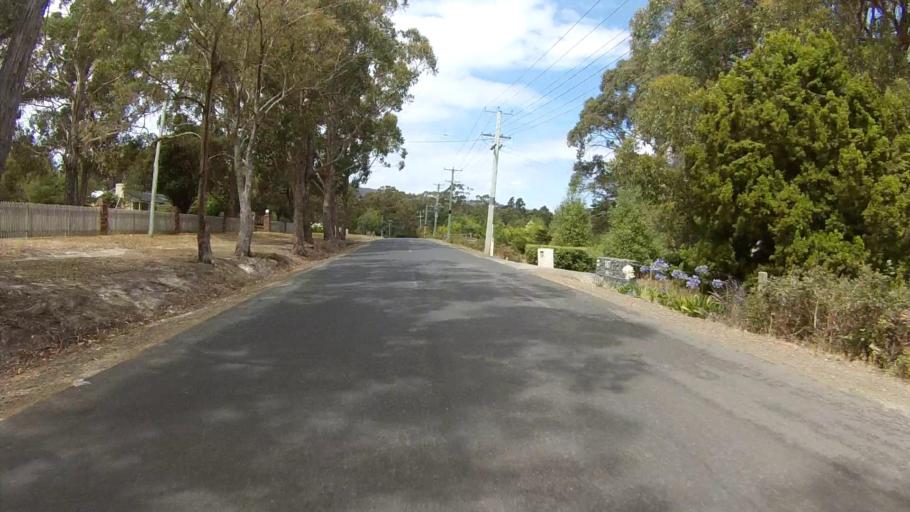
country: AU
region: Tasmania
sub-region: Kingborough
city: Blackmans Bay
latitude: -43.0128
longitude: 147.2887
